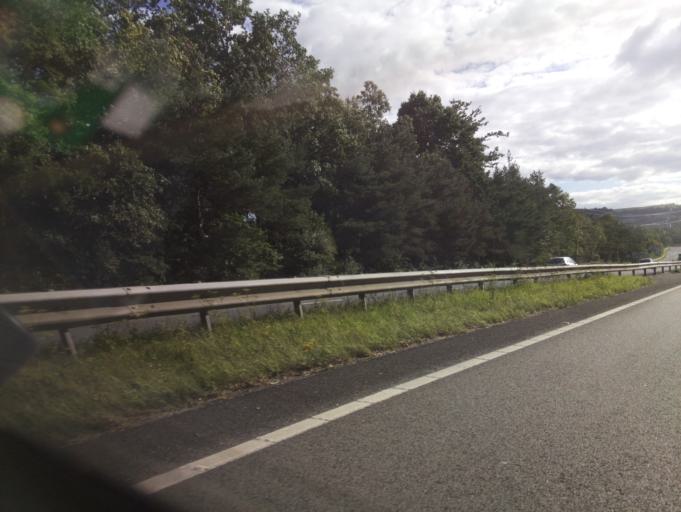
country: GB
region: England
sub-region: Devon
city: Bovey Tracey
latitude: 50.5682
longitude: -3.6502
